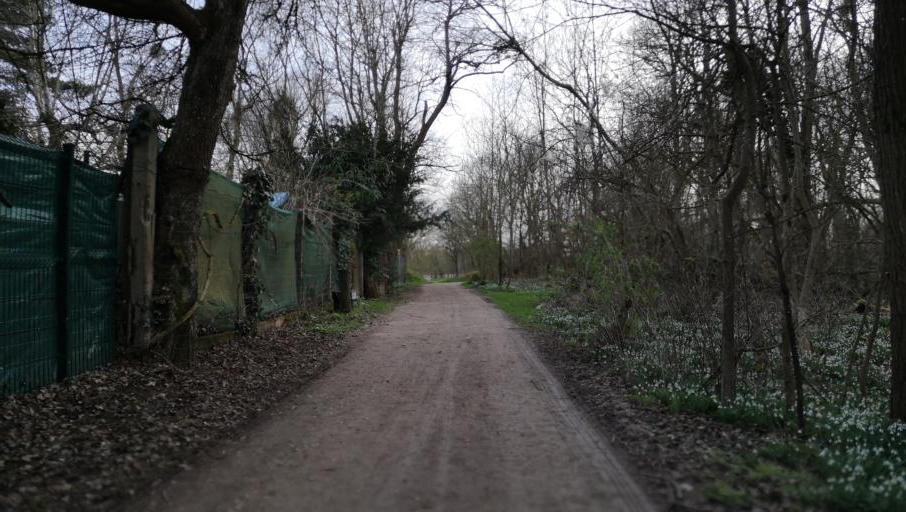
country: FR
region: Centre
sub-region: Departement du Loiret
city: La Chapelle-Saint-Mesmin
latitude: 47.8800
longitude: 1.8304
